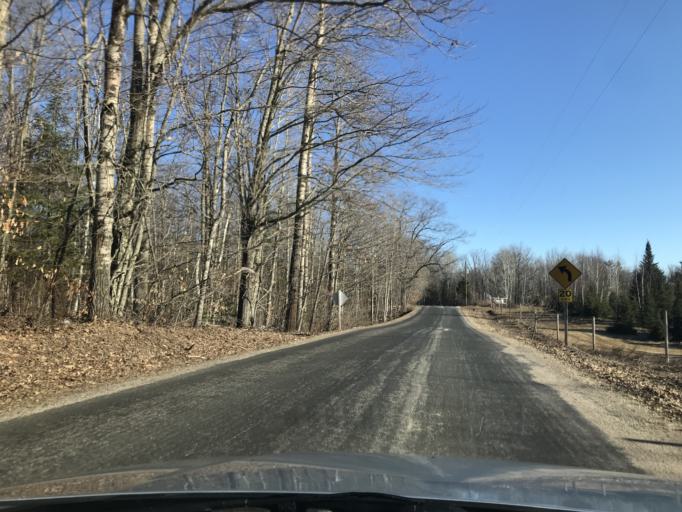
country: US
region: Wisconsin
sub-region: Marinette County
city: Niagara
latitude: 45.3727
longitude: -88.0192
